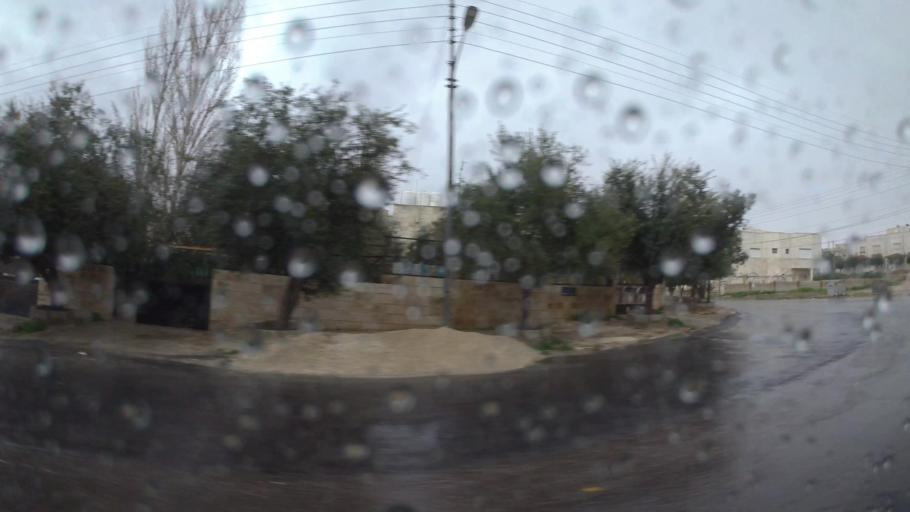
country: JO
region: Amman
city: Amman
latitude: 32.0040
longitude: 35.9591
